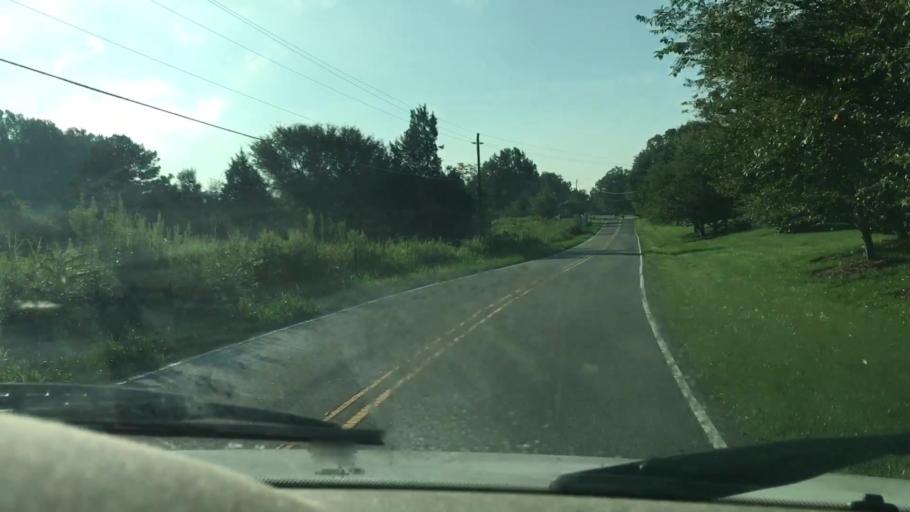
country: US
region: North Carolina
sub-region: Mecklenburg County
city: Huntersville
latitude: 35.4393
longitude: -80.8191
